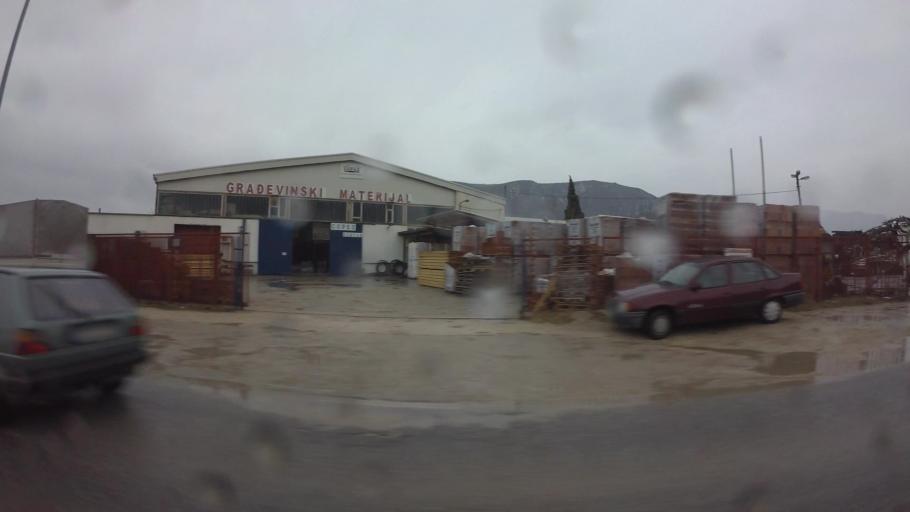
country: BA
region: Federation of Bosnia and Herzegovina
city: Rodoc
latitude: 43.3188
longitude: 17.8302
